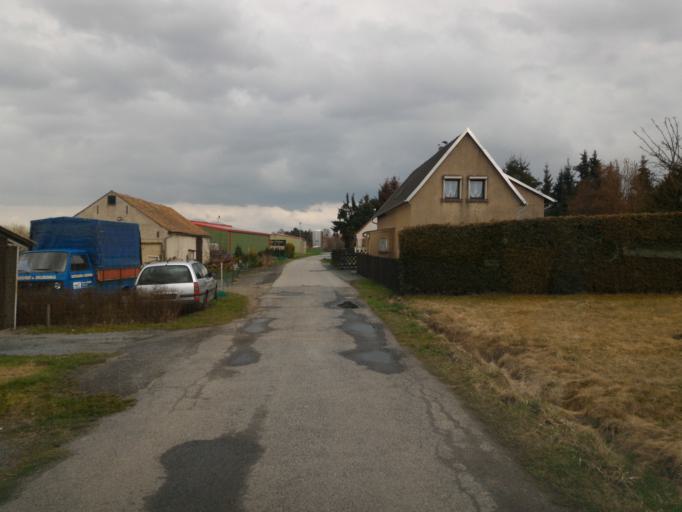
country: DE
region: Saxony
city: Neugersdorf
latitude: 50.9797
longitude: 14.6228
